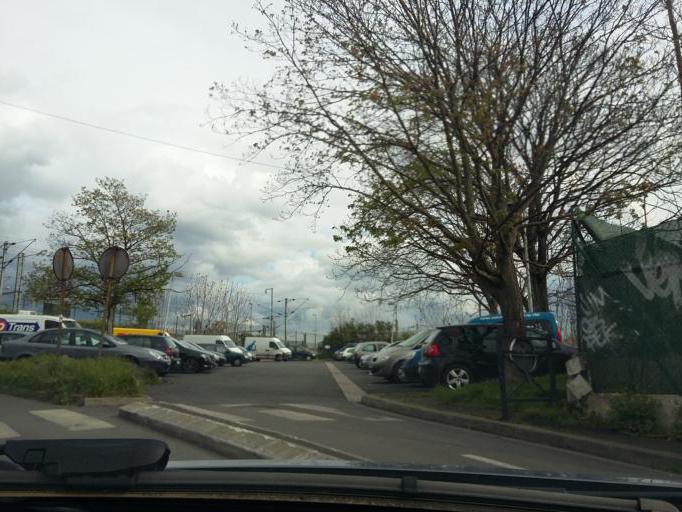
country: FR
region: Ile-de-France
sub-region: Departement de Seine-Saint-Denis
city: Saint-Denis
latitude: 48.9344
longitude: 2.3445
